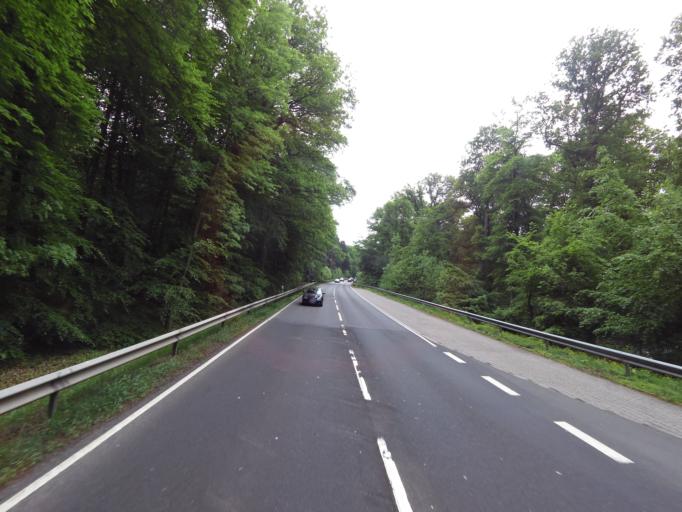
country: DE
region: Rheinland-Pfalz
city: Waldesch
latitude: 50.3108
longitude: 7.5541
